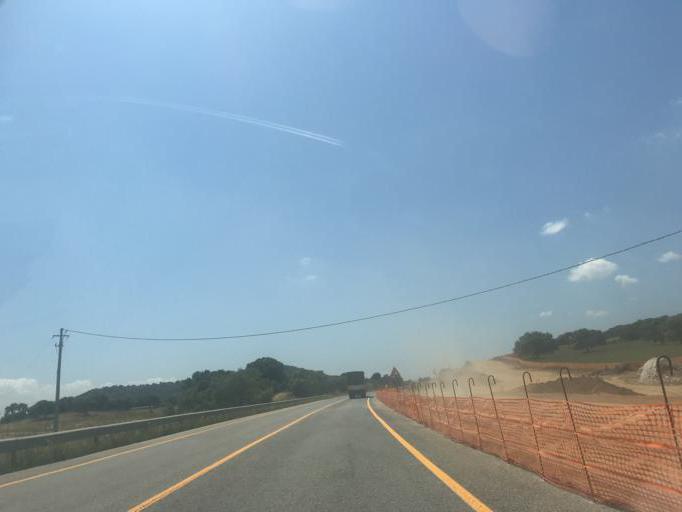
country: IT
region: Sardinia
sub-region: Provincia di Olbia-Tempio
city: Berchidda
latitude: 40.7789
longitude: 9.2381
